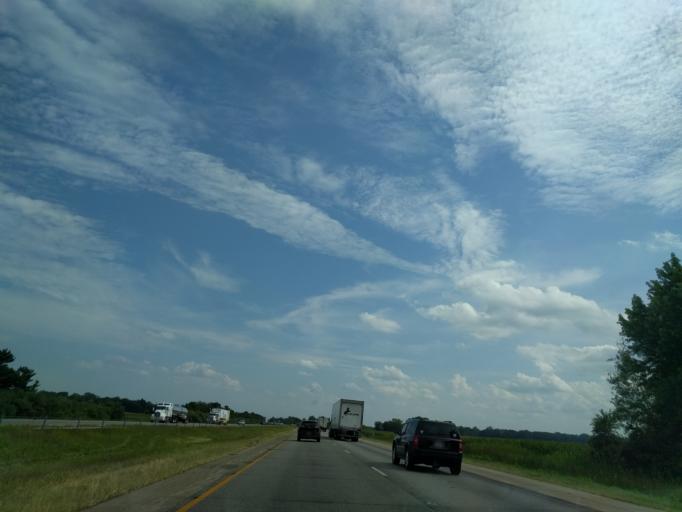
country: US
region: Indiana
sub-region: Jasper County
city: Rensselaer
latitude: 40.9826
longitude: -87.2554
